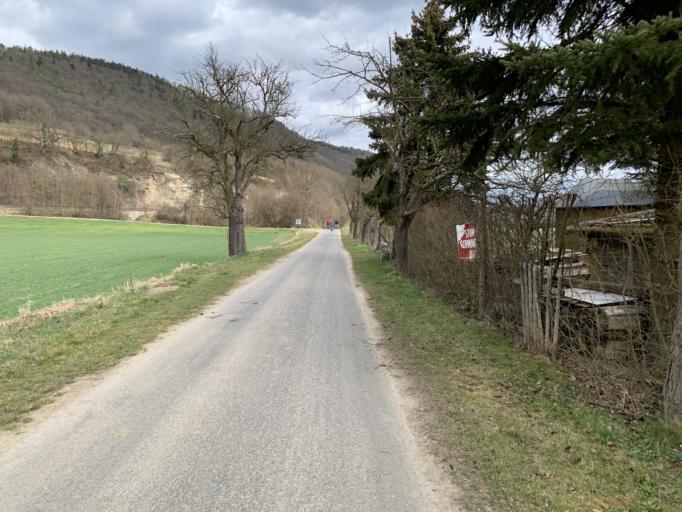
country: AT
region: Lower Austria
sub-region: Politischer Bezirk Melk
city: Emmersdorf an der Donau
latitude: 48.2658
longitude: 15.3677
